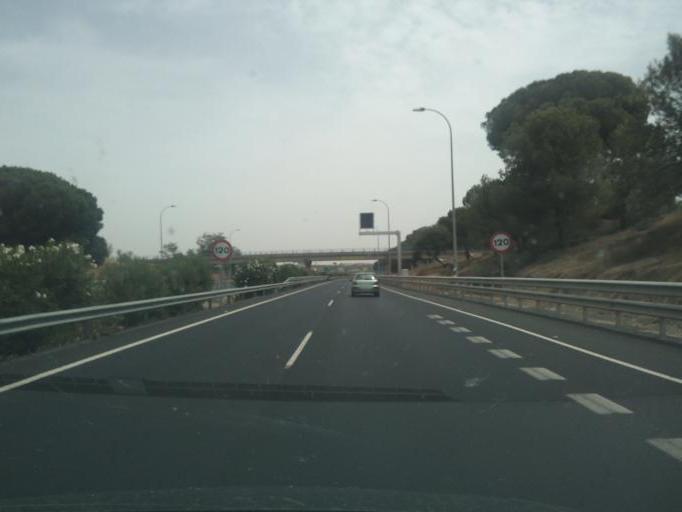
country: ES
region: Andalusia
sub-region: Provincia de Huelva
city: Bollullos par del Condado
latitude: 37.3590
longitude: -6.5319
